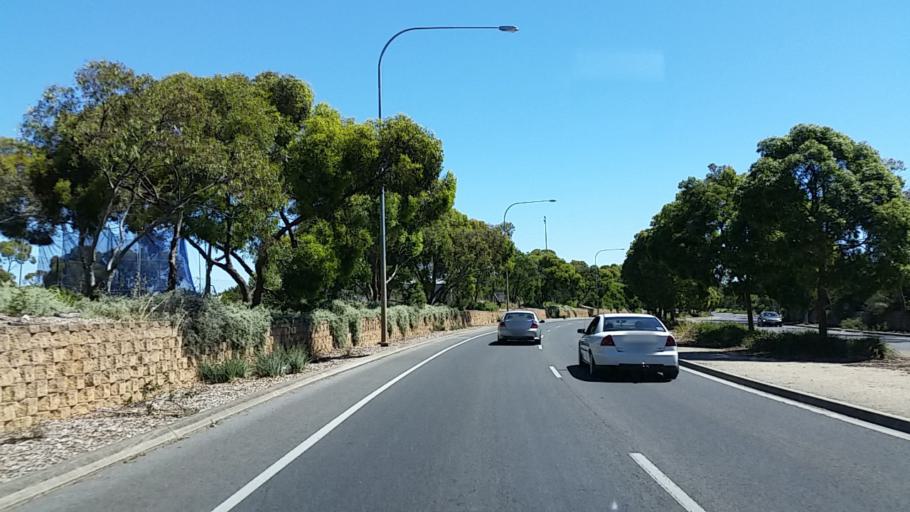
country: AU
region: South Australia
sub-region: City of West Torrens
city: Thebarton
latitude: -34.9273
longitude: 138.5790
